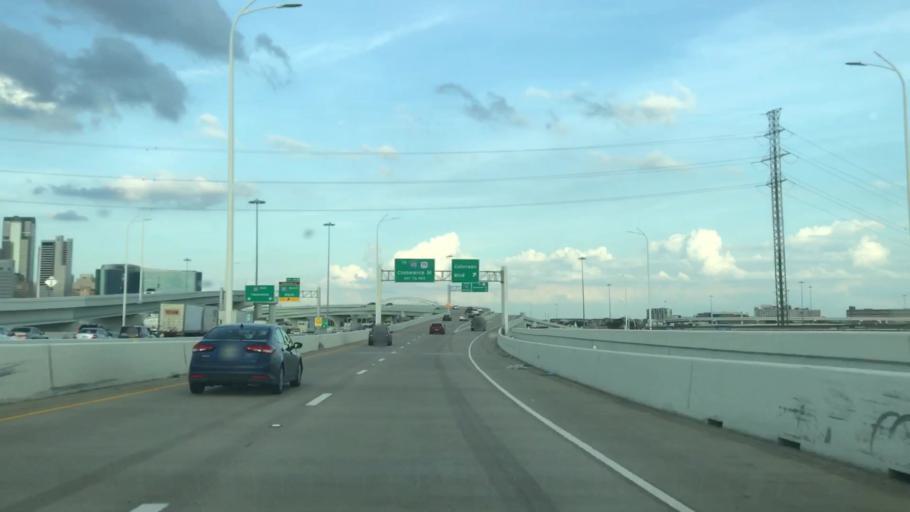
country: US
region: Texas
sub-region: Dallas County
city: Dallas
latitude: 32.7704
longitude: -96.8156
